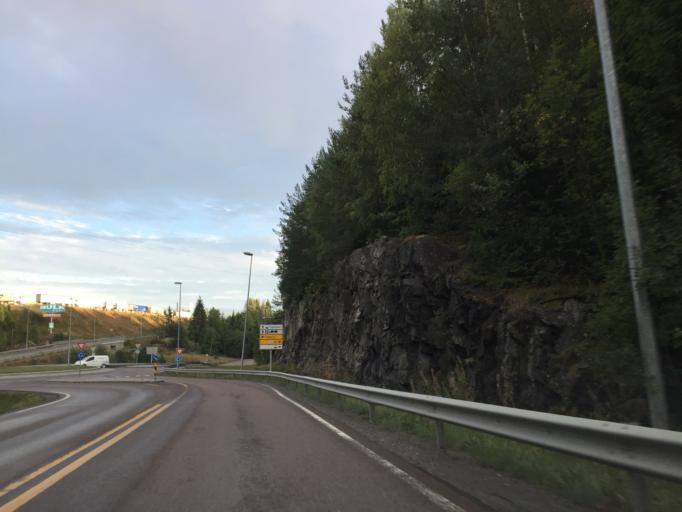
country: NO
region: Akershus
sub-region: Oppegard
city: Kolbotn
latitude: 59.7760
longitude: 10.8499
